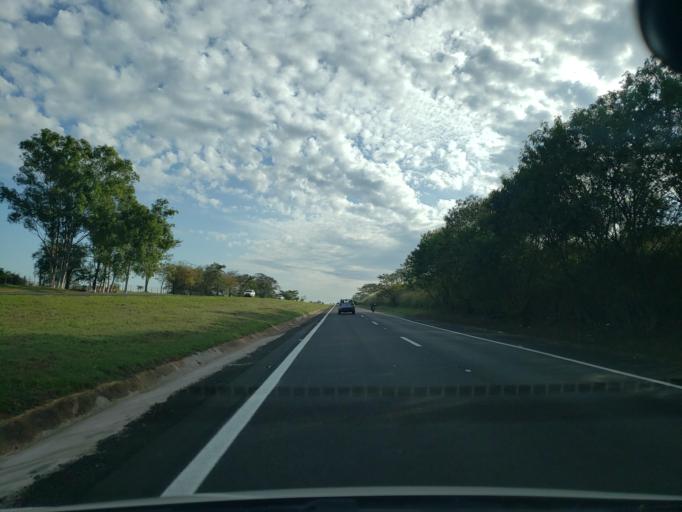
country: BR
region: Sao Paulo
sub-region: Guararapes
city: Guararapes
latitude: -21.2007
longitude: -50.5793
